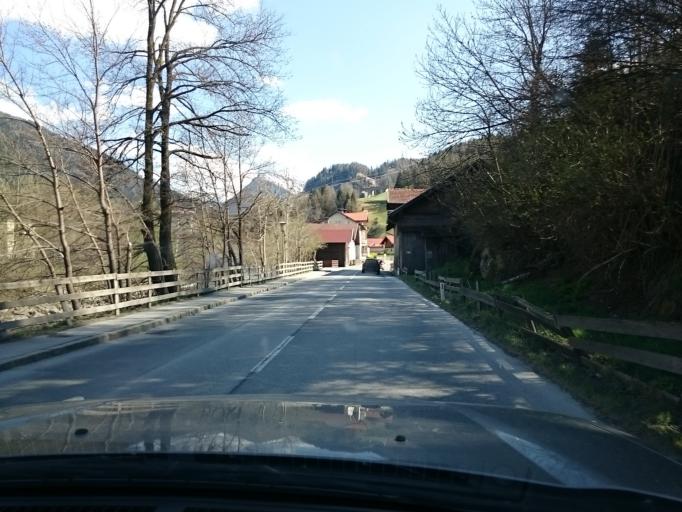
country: AT
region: Tyrol
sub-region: Politischer Bezirk Innsbruck Land
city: Steinach am Brenner
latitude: 47.0869
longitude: 11.4688
